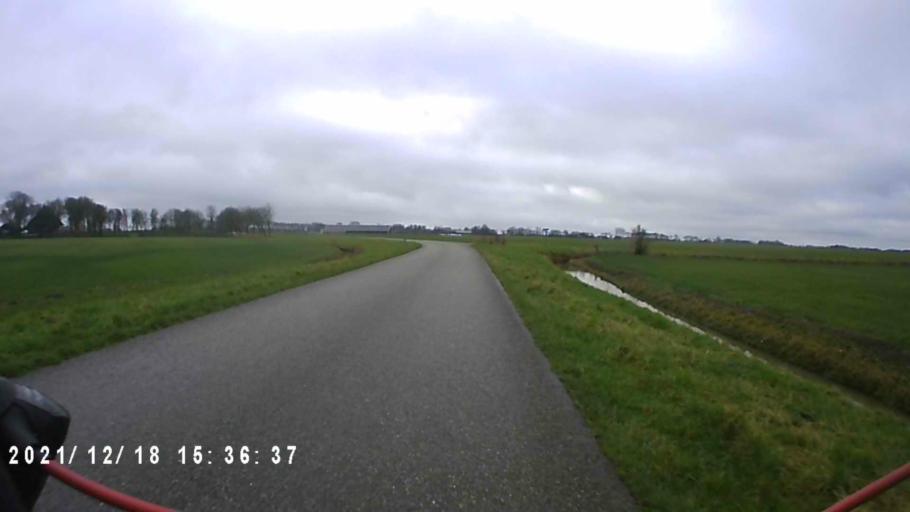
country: NL
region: Friesland
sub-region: Gemeente Dongeradeel
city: Anjum
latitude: 53.3418
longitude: 6.1268
